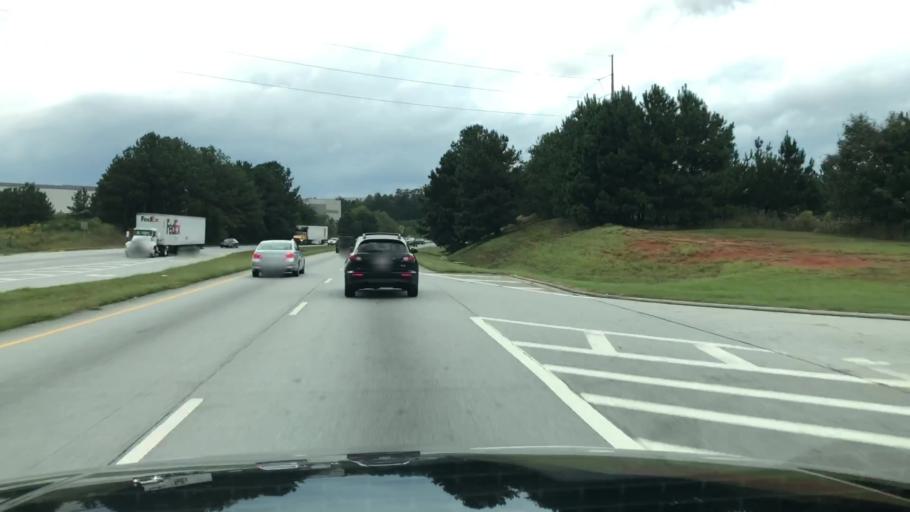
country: US
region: Georgia
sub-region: Cobb County
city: Mableton
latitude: 33.7423
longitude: -84.5879
